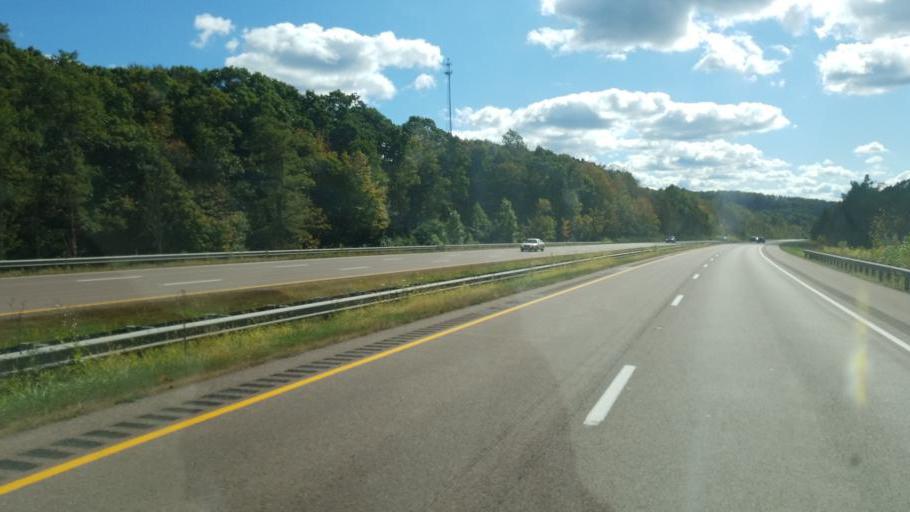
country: US
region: Maryland
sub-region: Garrett County
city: Oakland
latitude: 39.6712
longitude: -79.3853
